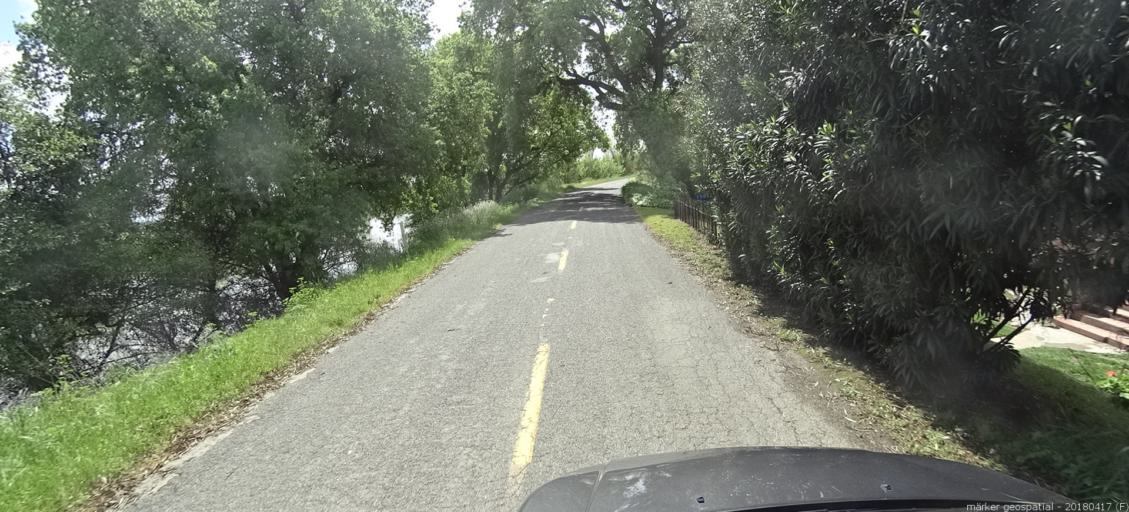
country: US
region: California
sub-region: Sacramento County
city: Walnut Grove
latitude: 38.2125
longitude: -121.5375
